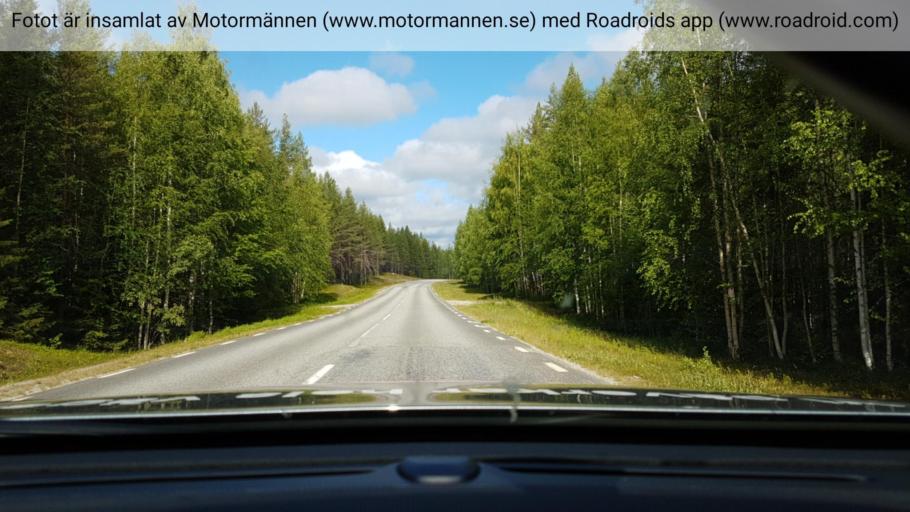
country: SE
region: Vaesterbotten
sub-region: Lycksele Kommun
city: Lycksele
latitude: 64.7964
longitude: 18.9632
